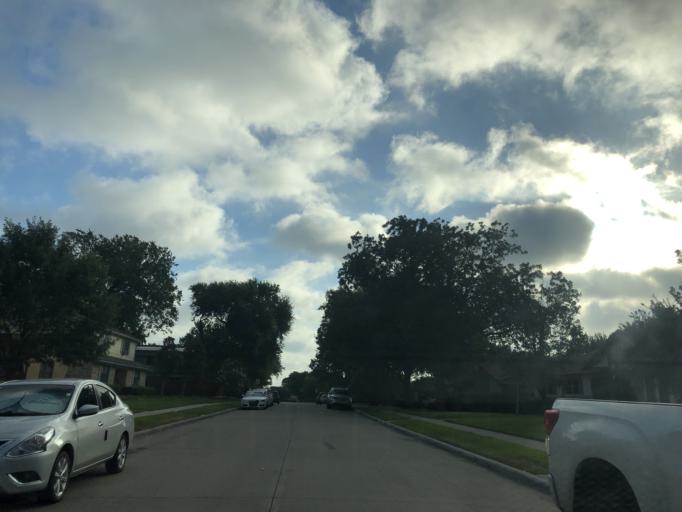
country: US
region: Texas
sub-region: Dallas County
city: Garland
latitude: 32.8579
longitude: -96.6413
